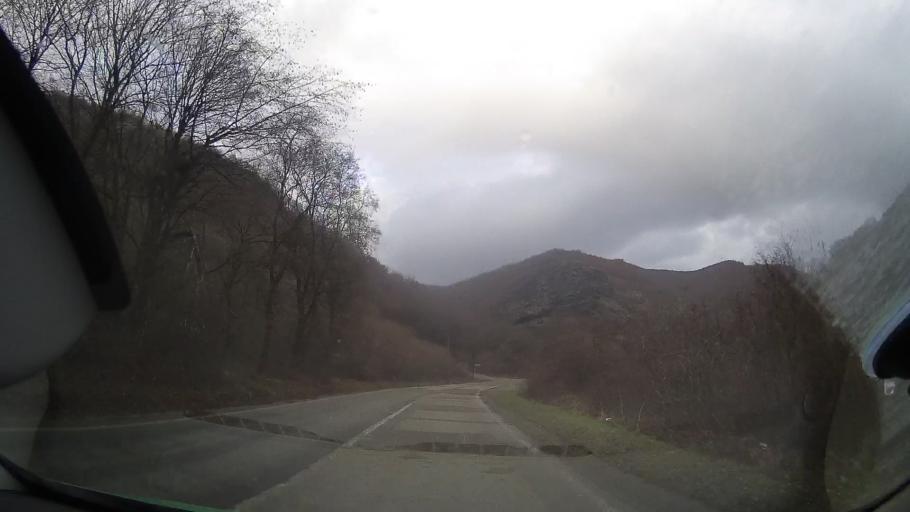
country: RO
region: Cluj
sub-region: Comuna Moldovenesti
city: Moldovenesti
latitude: 46.5057
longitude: 23.6387
